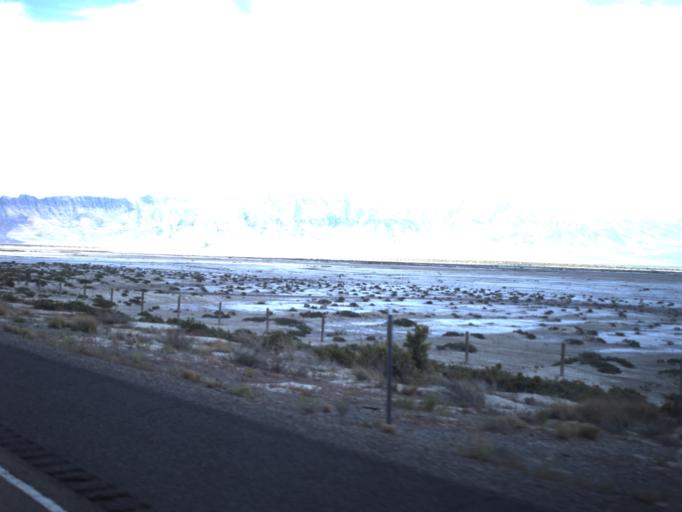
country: US
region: Utah
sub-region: Tooele County
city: Grantsville
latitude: 40.7568
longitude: -112.7651
